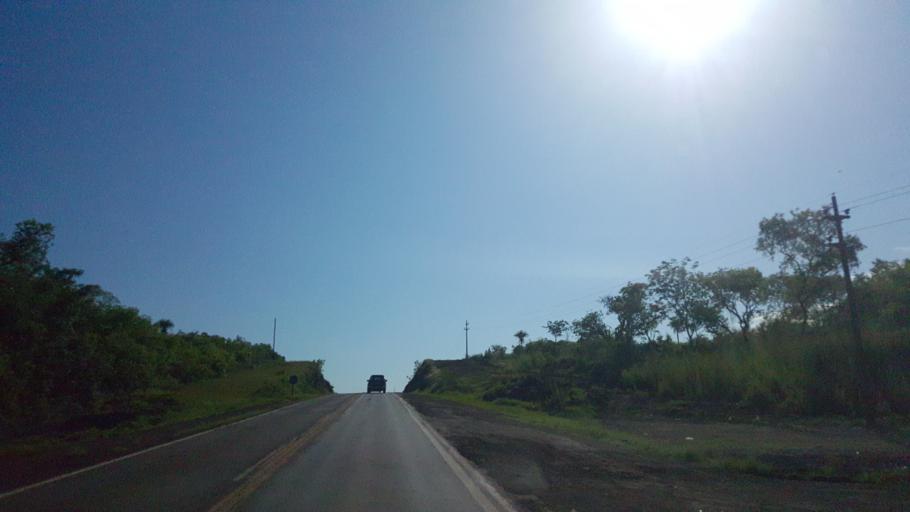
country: AR
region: Misiones
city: Santa Ana
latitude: -27.3718
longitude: -55.5674
